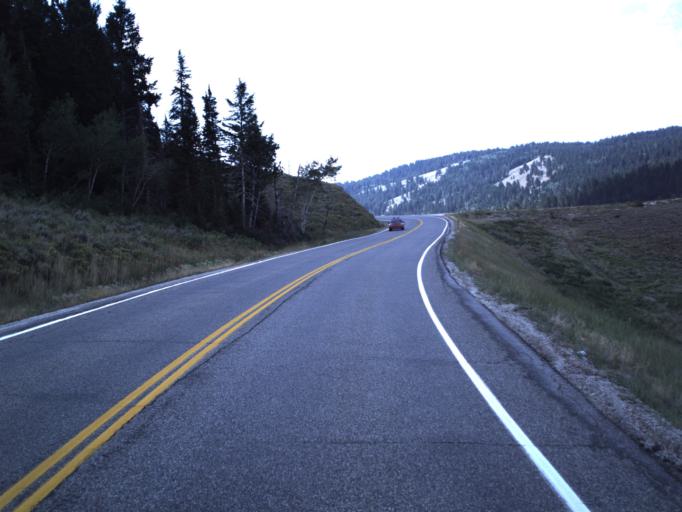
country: US
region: Idaho
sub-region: Bear Lake County
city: Paris
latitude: 41.9360
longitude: -111.4814
